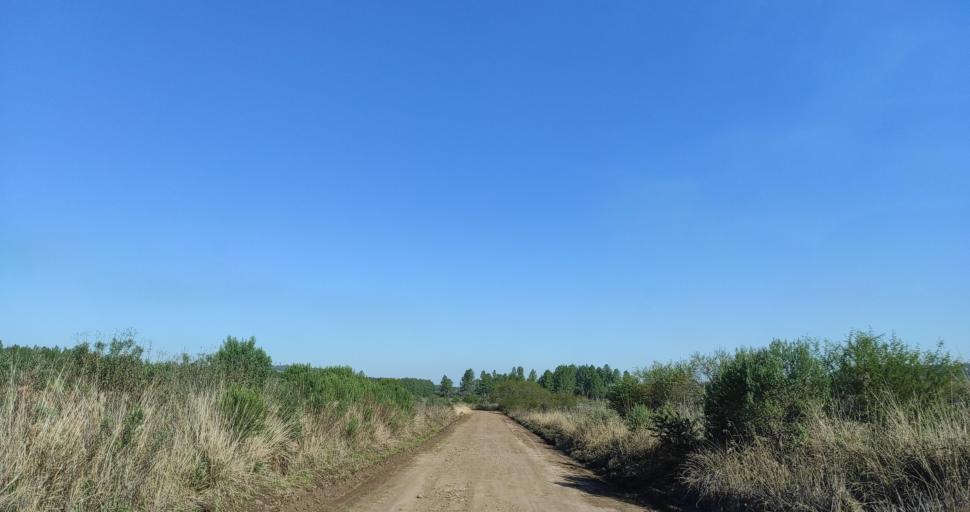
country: AR
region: Misiones
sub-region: Departamento de Apostoles
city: San Jose
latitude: -27.6728
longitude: -55.6611
